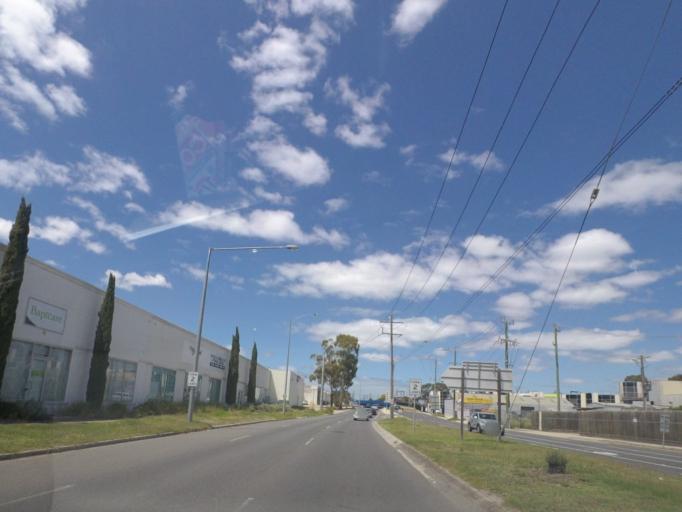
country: AU
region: Victoria
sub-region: Brimbank
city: Sunshine North
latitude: -37.7793
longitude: 144.8285
